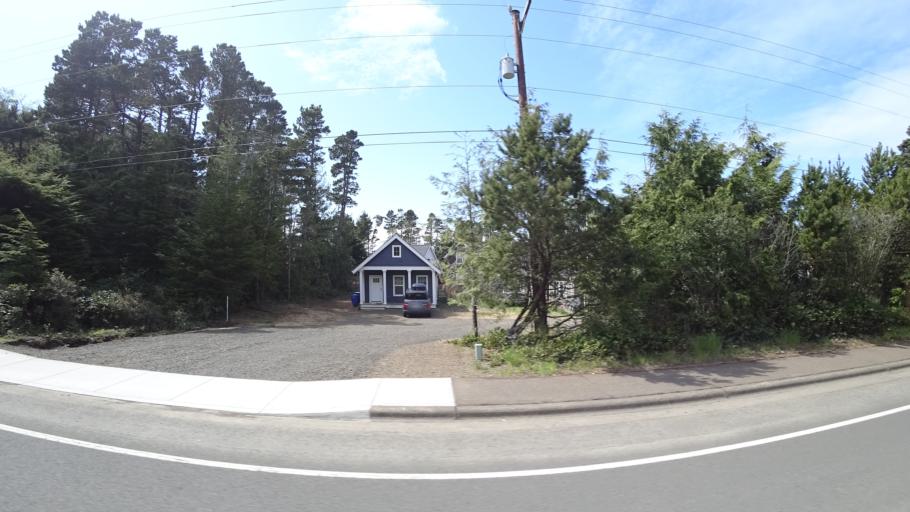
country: US
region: Oregon
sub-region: Lincoln County
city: Lincoln Beach
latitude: 44.8615
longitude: -124.0379
